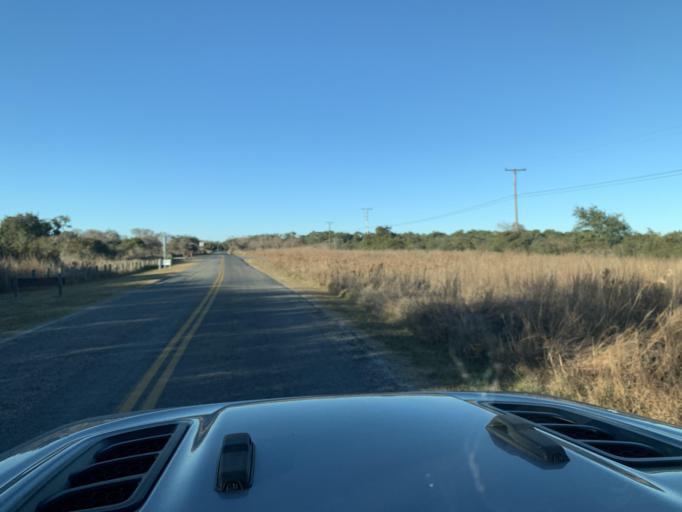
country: US
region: Texas
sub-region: Aransas County
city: Fulton
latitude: 28.1346
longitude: -96.9843
